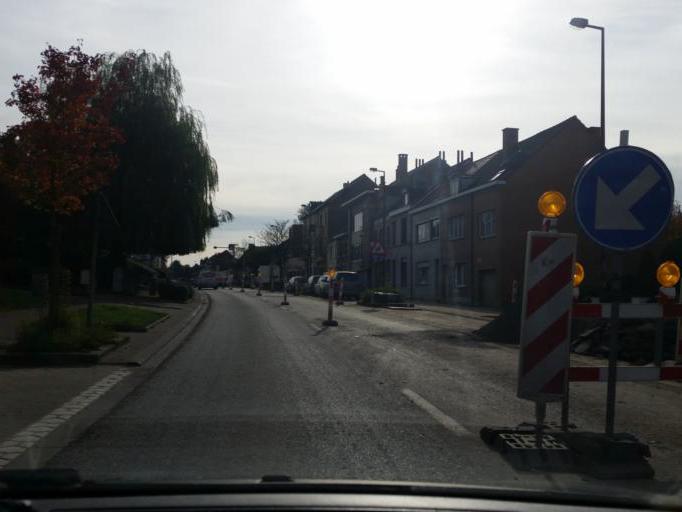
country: BE
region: Flanders
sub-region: Provincie Vlaams-Brabant
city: Grimbergen
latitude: 50.9336
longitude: 4.3642
